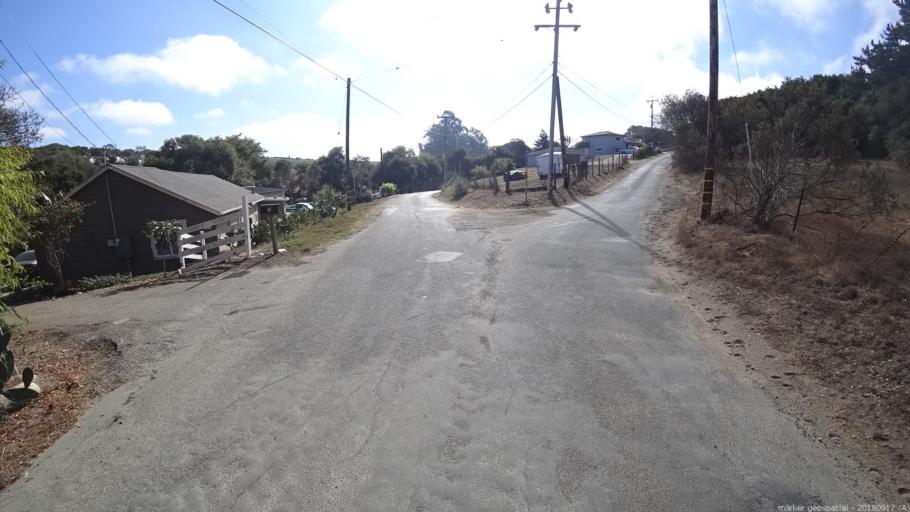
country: US
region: California
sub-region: Monterey County
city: Elkhorn
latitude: 36.7884
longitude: -121.7208
